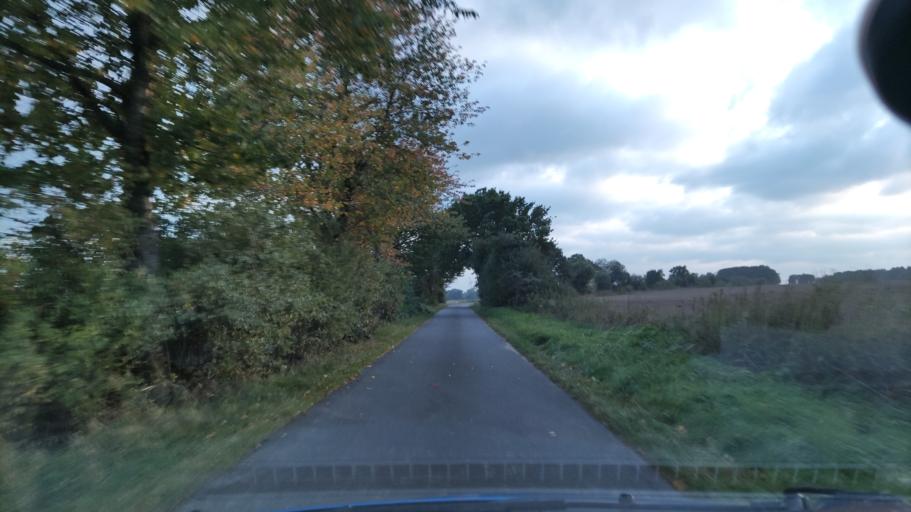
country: DE
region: Lower Saxony
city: Tosterglope
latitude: 53.2207
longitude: 10.8289
